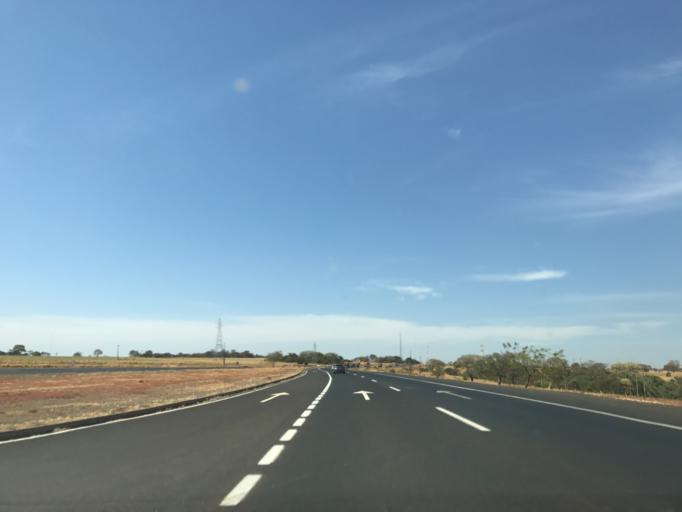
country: BR
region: Minas Gerais
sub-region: Centralina
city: Centralina
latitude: -18.7603
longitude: -49.0762
